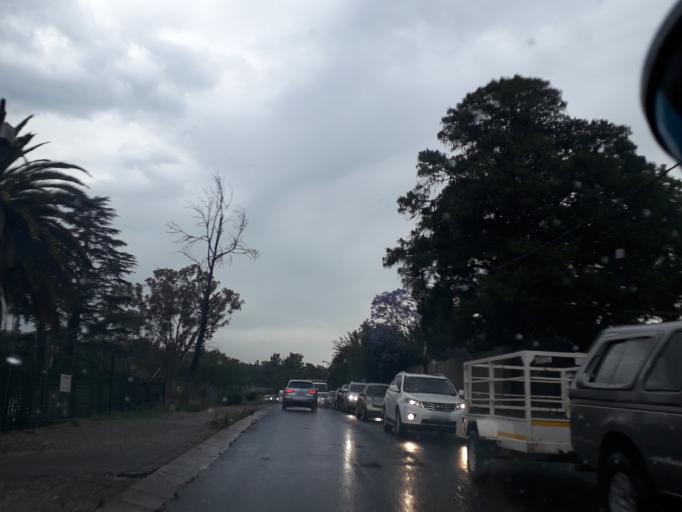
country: ZA
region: Gauteng
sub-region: City of Johannesburg Metropolitan Municipality
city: Johannesburg
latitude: -26.0811
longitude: 27.9878
